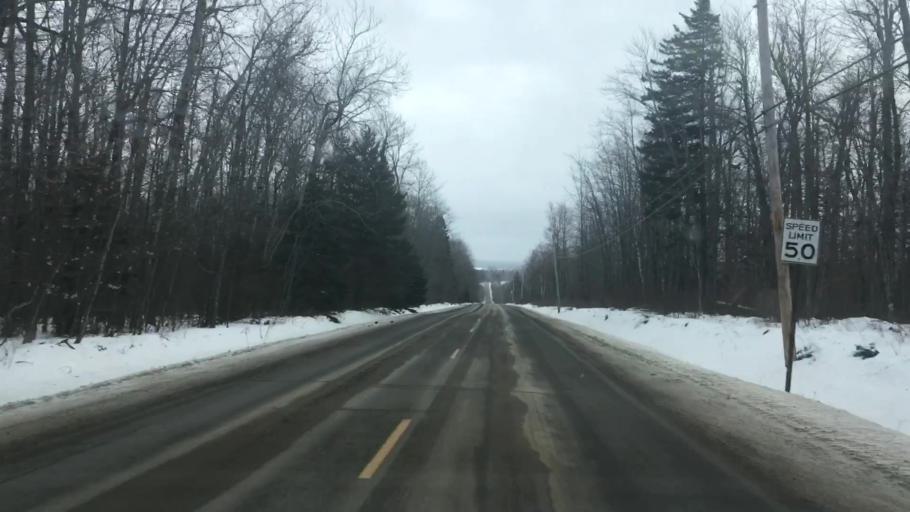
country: US
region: Maine
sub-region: Washington County
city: East Machias
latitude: 44.9756
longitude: -67.4508
